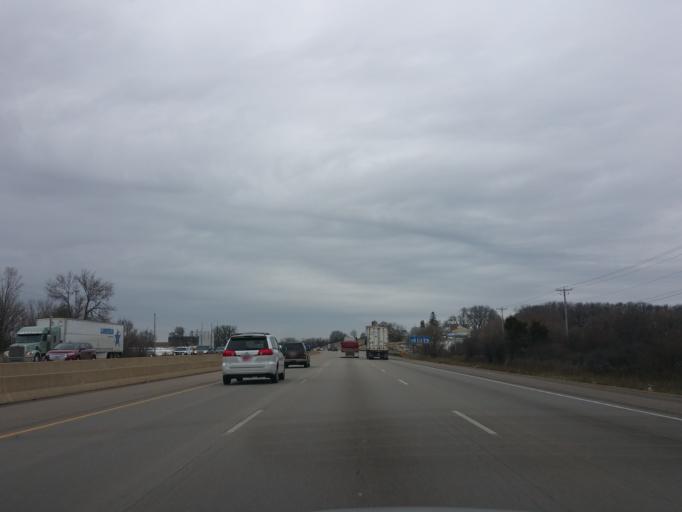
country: US
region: Wisconsin
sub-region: Dane County
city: Windsor
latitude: 43.1530
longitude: -89.3059
